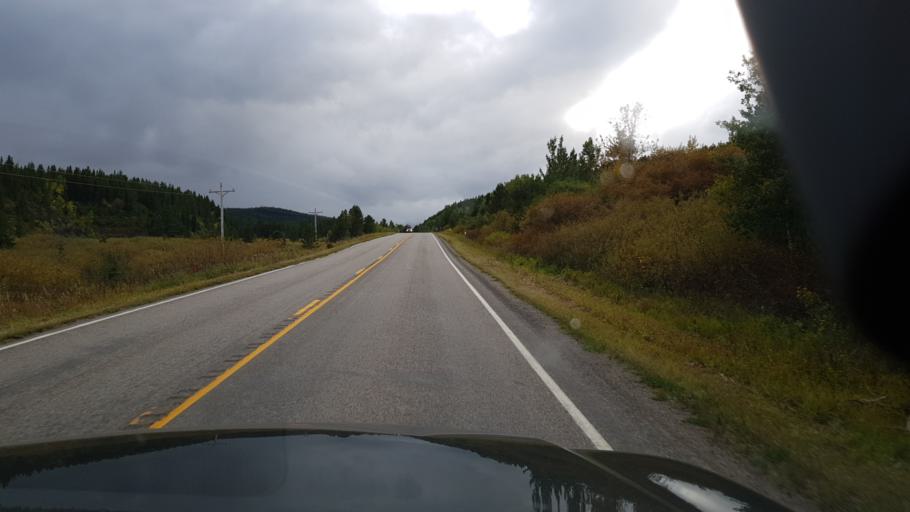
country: US
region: Montana
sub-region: Glacier County
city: South Browning
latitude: 48.3443
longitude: -113.3197
